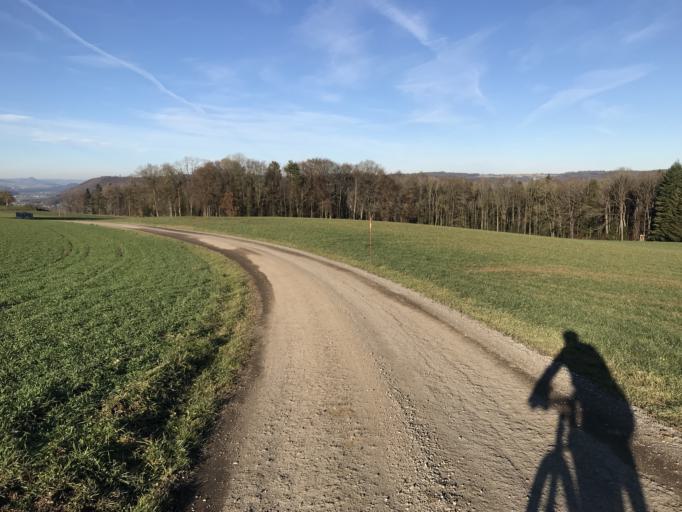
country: CH
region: Thurgau
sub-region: Frauenfeld District
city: Eschenz
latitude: 47.6362
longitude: 8.8567
